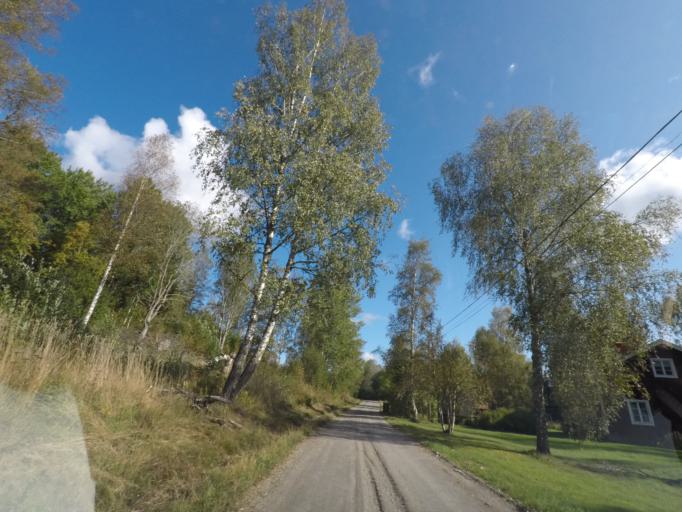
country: SE
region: Vaestmanland
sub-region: Skinnskattebergs Kommun
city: Skinnskatteberg
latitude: 59.8260
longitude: 15.5189
